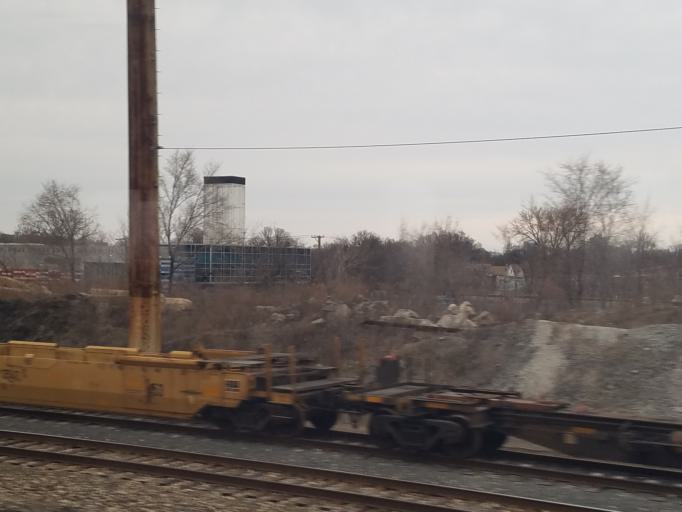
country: US
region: Illinois
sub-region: Cook County
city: Chicago
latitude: 41.7656
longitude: -87.5956
